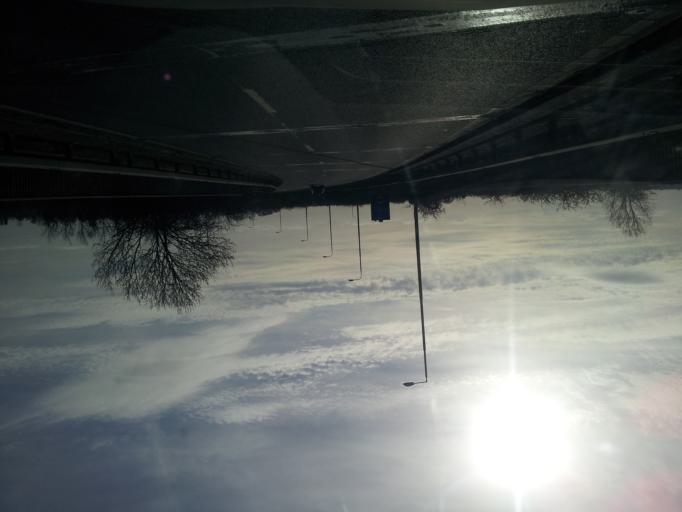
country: GB
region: England
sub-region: Central Bedfordshire
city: Tempsford
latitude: 52.1769
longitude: -0.3006
